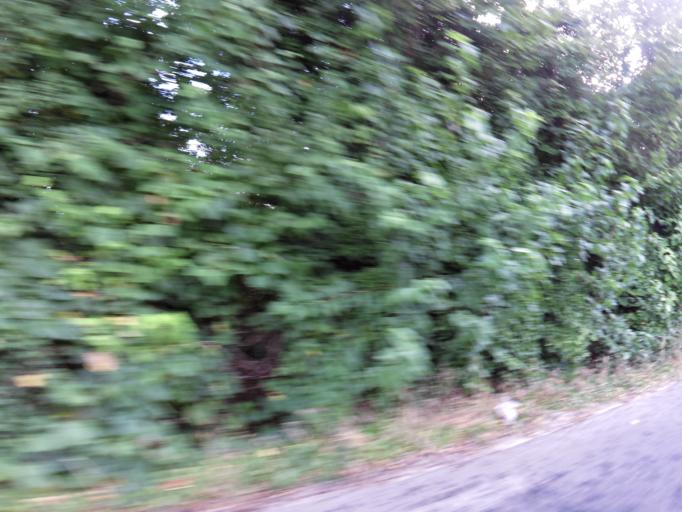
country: FR
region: Languedoc-Roussillon
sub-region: Departement du Gard
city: Saint-Mamert-du-Gard
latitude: 43.9105
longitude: 4.1980
